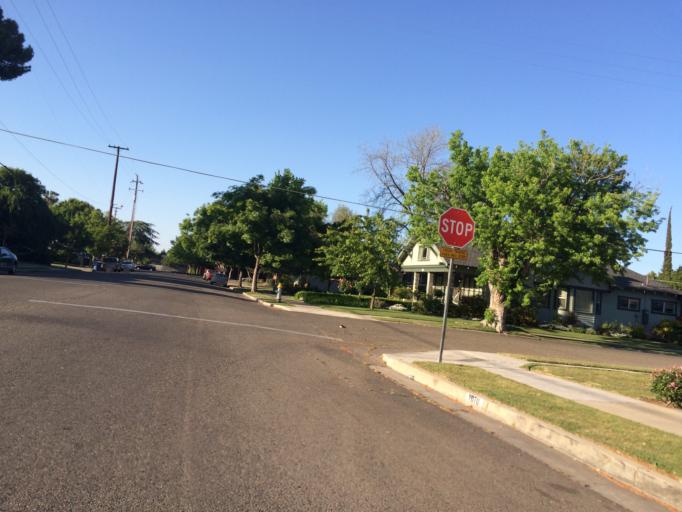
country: US
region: California
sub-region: Fresno County
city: Fresno
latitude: 36.7564
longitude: -119.7975
